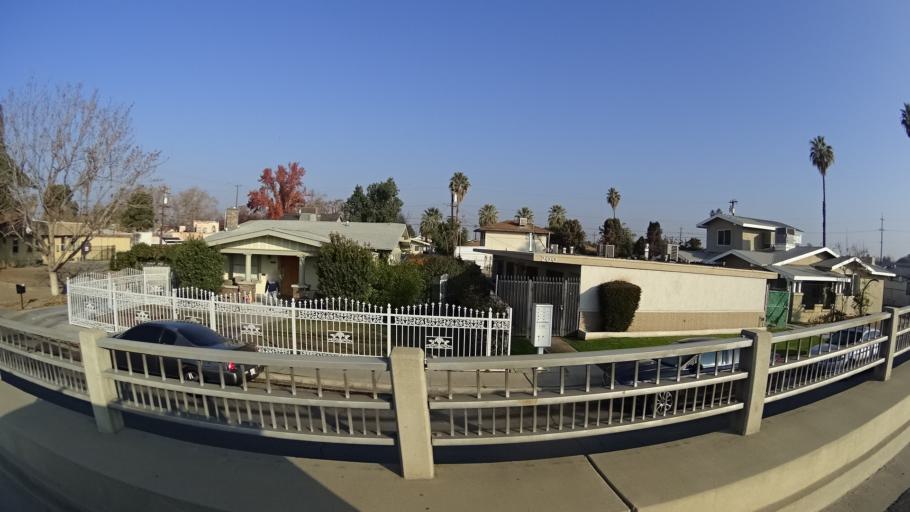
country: US
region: California
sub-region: Kern County
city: Bakersfield
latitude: 35.3737
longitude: -119.0042
